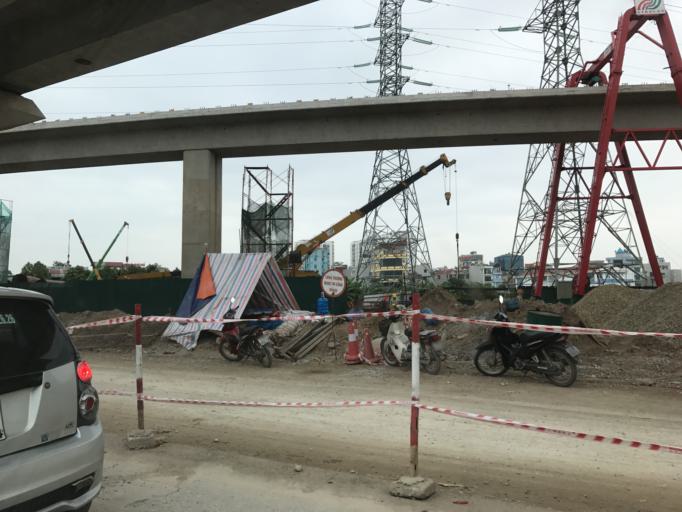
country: VN
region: Ha Noi
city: Ha Dong
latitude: 20.9539
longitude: 105.7538
